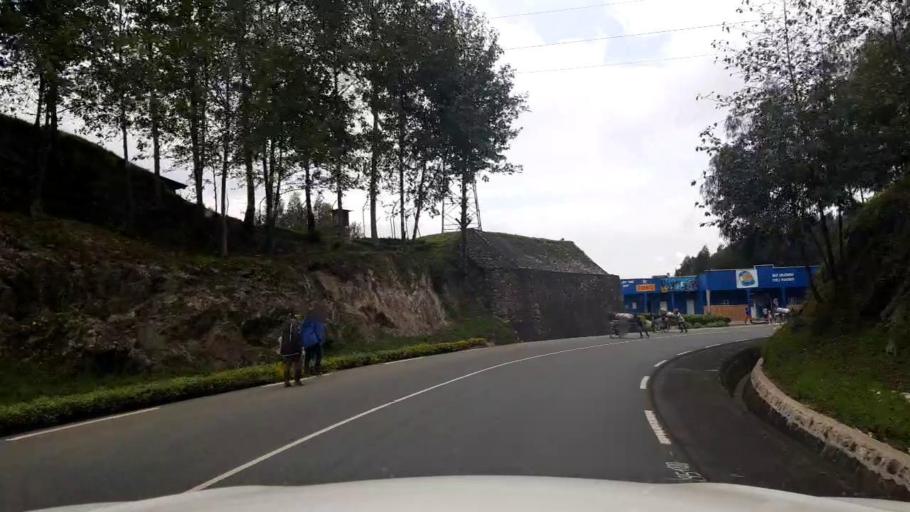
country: RW
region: Northern Province
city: Musanze
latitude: -1.6583
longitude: 29.5126
